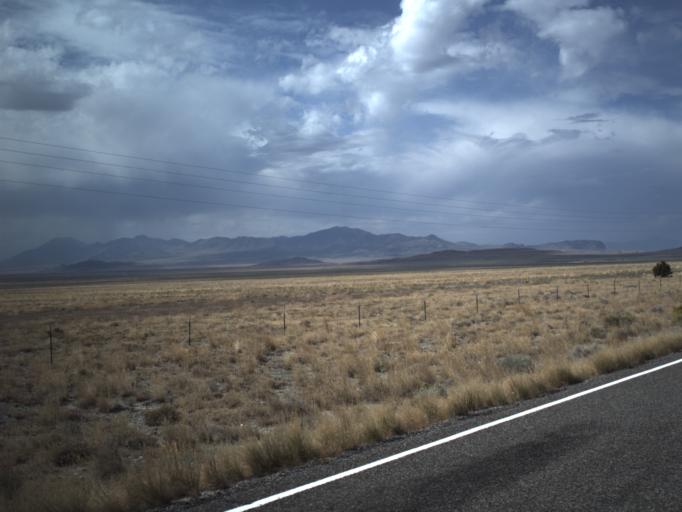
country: US
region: Utah
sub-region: Tooele County
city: Wendover
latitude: 41.4319
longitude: -113.7910
